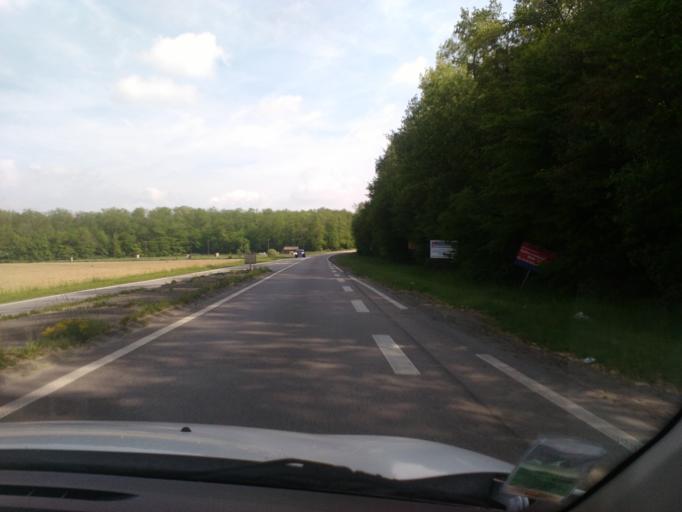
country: FR
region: Lorraine
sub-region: Departement des Vosges
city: Golbey
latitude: 48.2095
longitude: 6.4193
